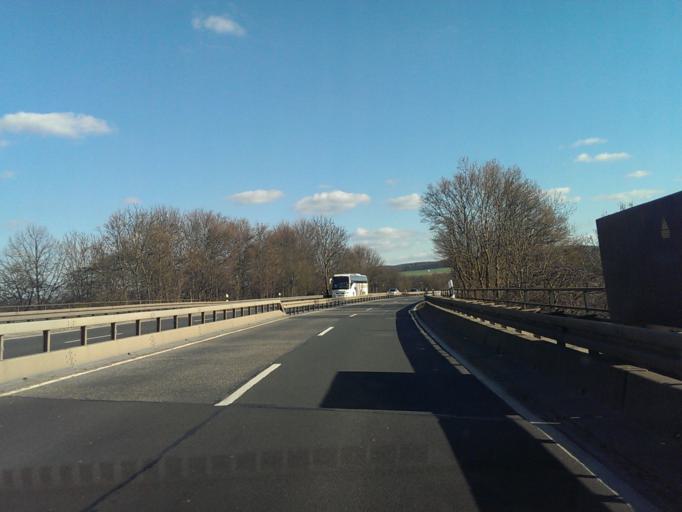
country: DE
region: Lower Saxony
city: Hildesheim
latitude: 52.1617
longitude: 9.9701
